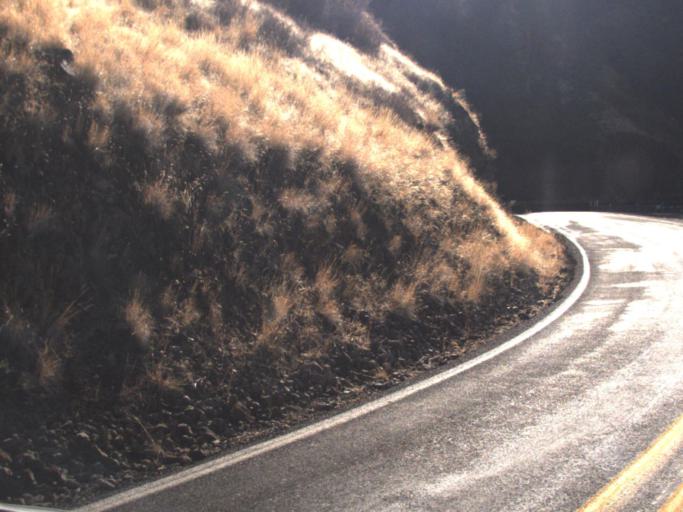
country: US
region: Washington
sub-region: Asotin County
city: Asotin
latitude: 46.0691
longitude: -117.2228
